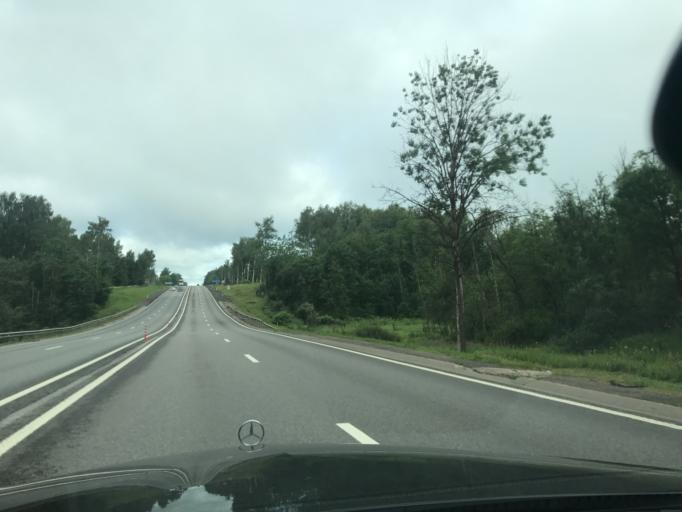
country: RU
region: Smolensk
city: Gagarin
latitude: 55.4989
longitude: 35.2478
